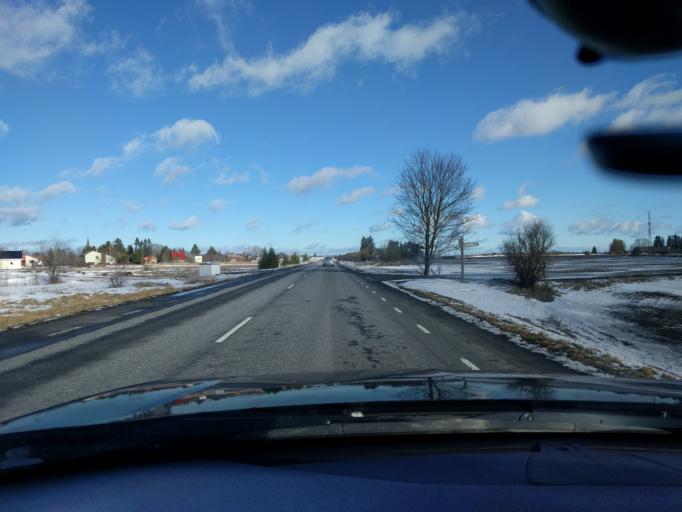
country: EE
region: Harju
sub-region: Raasiku vald
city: Raasiku
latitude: 59.3667
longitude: 25.1901
